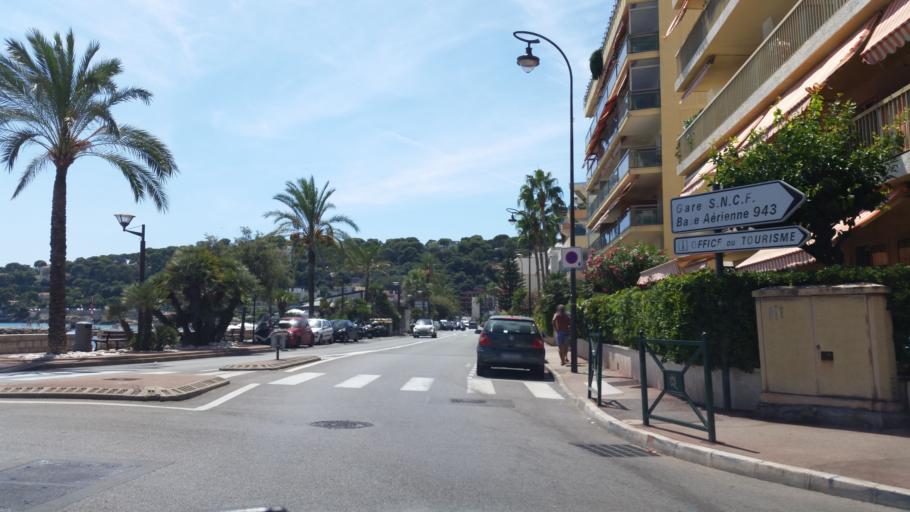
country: FR
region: Provence-Alpes-Cote d'Azur
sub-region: Departement des Alpes-Maritimes
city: Roquebrune-Cap-Martin
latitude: 43.7603
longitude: 7.4834
